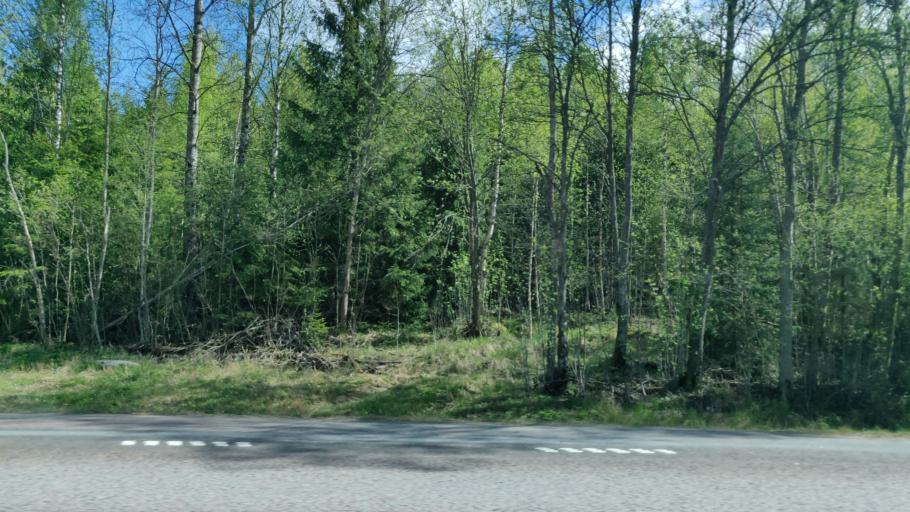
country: SE
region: Vaermland
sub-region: Karlstads Kommun
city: Molkom
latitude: 59.5728
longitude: 13.6674
